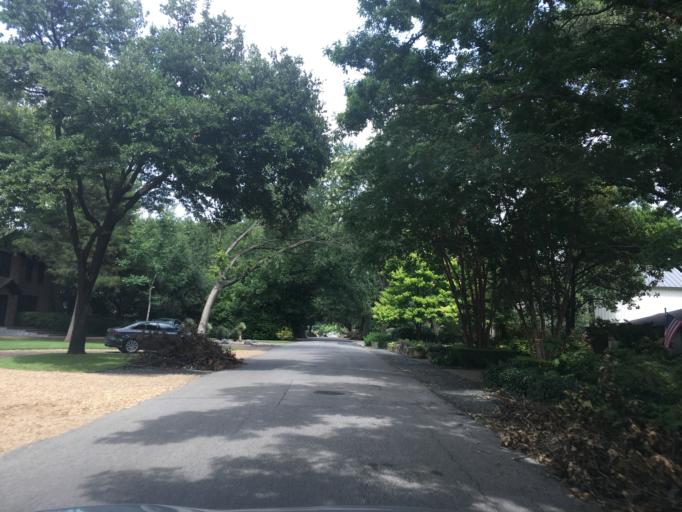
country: US
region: Texas
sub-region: Dallas County
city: University Park
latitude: 32.8863
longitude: -96.7984
